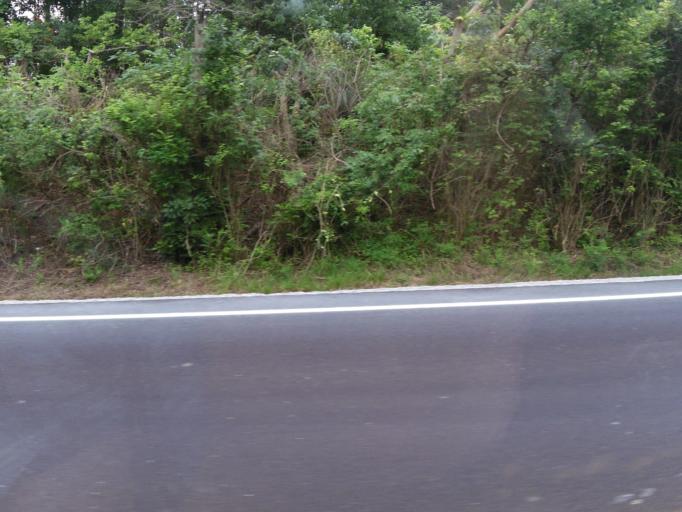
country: US
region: Ohio
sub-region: Clinton County
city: Blanchester
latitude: 39.1907
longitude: -83.9332
